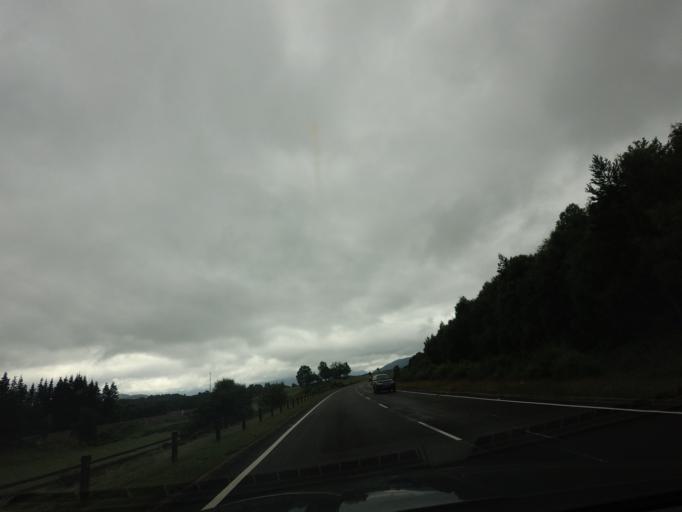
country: GB
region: Scotland
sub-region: Highland
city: Aviemore
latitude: 57.2364
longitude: -3.8090
